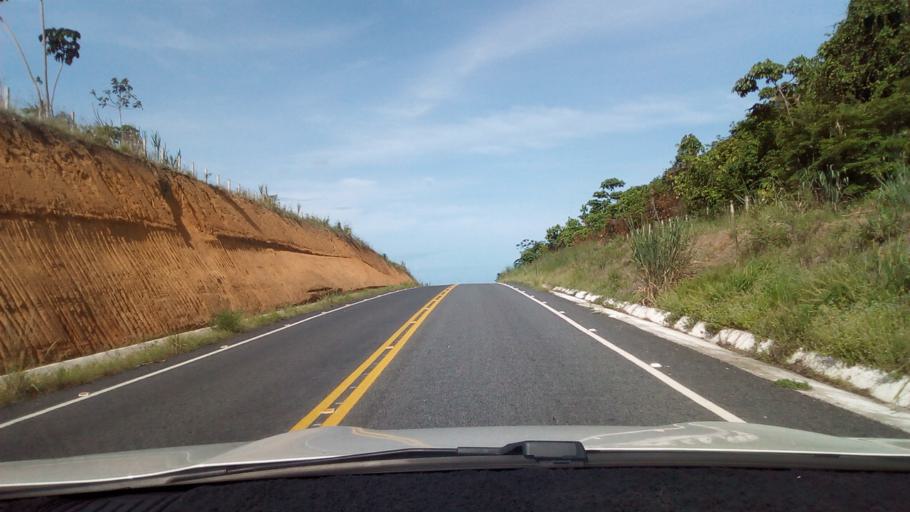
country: BR
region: Paraiba
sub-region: Bayeux
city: Bayeux
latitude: -7.0626
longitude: -34.9174
